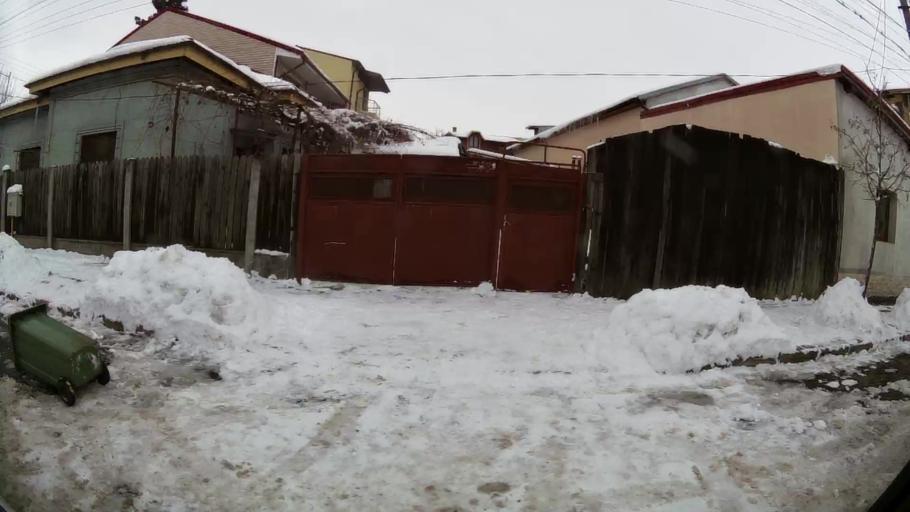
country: RO
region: Bucuresti
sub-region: Municipiul Bucuresti
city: Bucuresti
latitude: 44.3969
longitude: 26.1054
